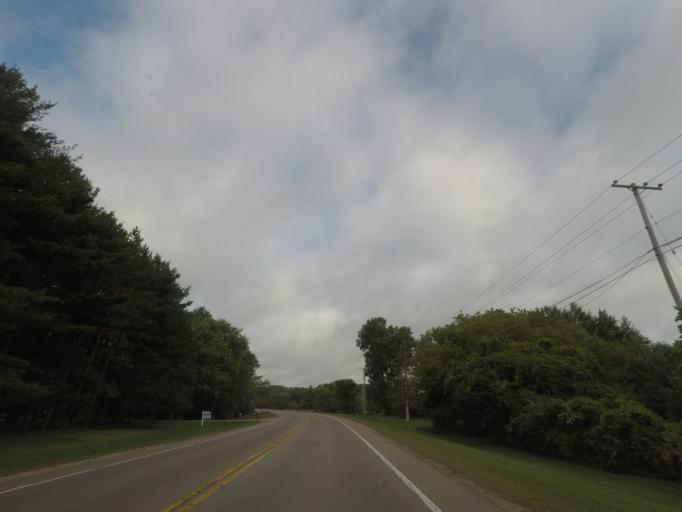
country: US
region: Wisconsin
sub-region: Waukesha County
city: Dousman
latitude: 43.0275
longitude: -88.5079
